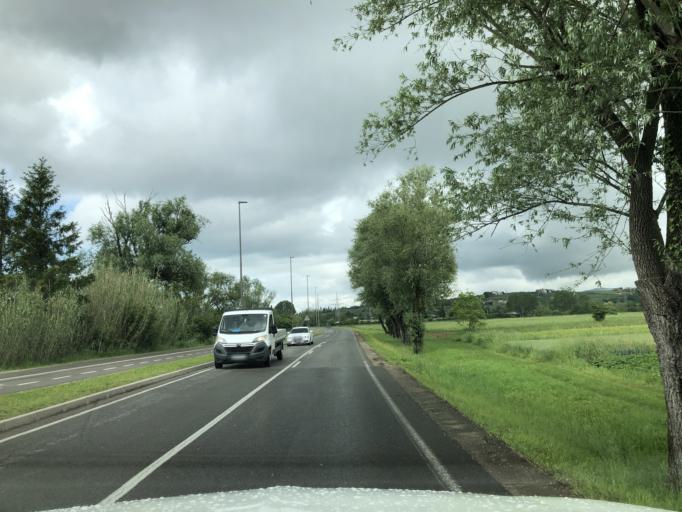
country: SI
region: Koper-Capodistria
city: Koper
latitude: 45.5234
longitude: 13.7407
